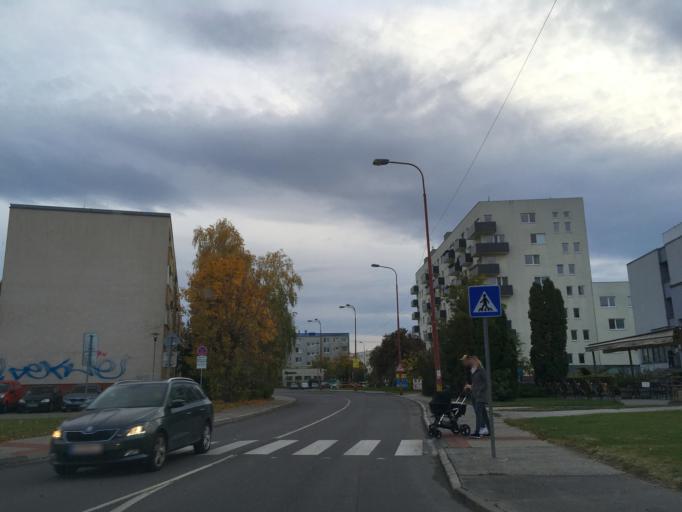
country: SK
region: Bratislavsky
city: Dunajska Luzna
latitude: 48.1413
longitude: 17.1971
